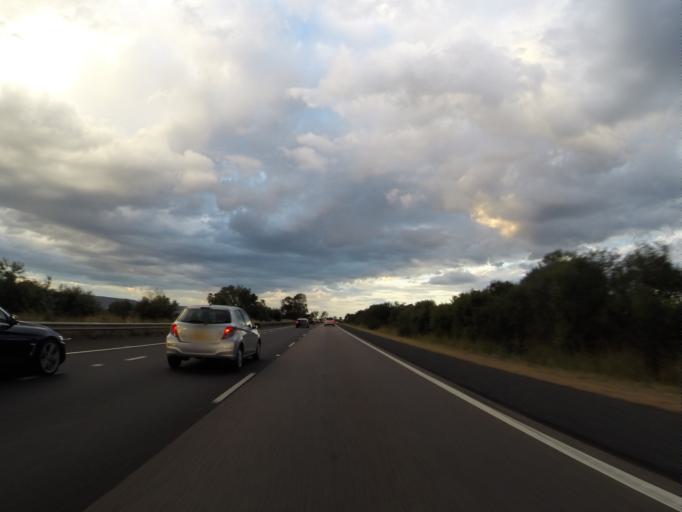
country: AU
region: New South Wales
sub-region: Wollondilly
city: Douglas Park
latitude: -34.2242
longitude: 150.6724
